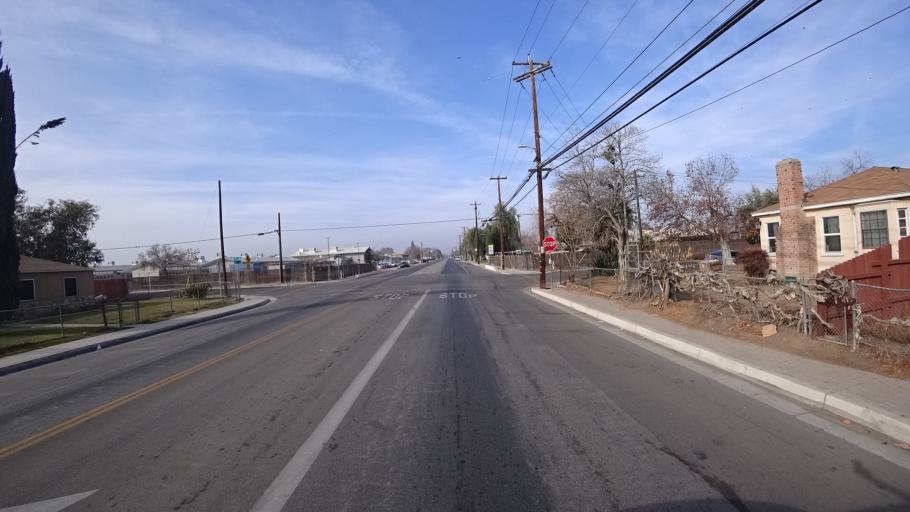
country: US
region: California
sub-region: Kern County
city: Bakersfield
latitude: 35.3608
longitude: -119.0070
